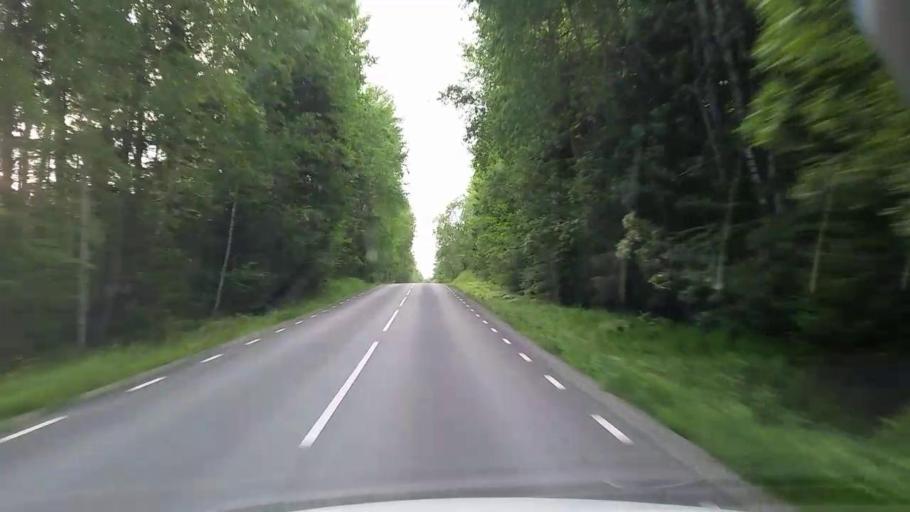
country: SE
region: Vaestmanland
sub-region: Kopings Kommun
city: Kolsva
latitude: 59.7253
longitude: 15.8318
